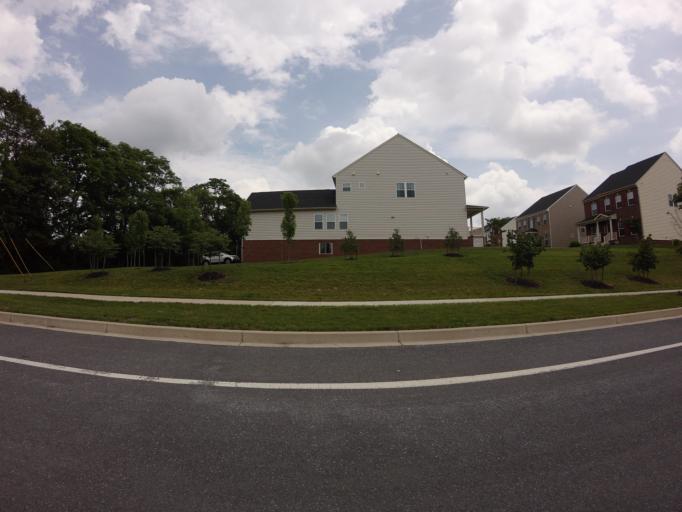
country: US
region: Maryland
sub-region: Frederick County
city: Ballenger Creek
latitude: 39.3708
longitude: -77.4459
